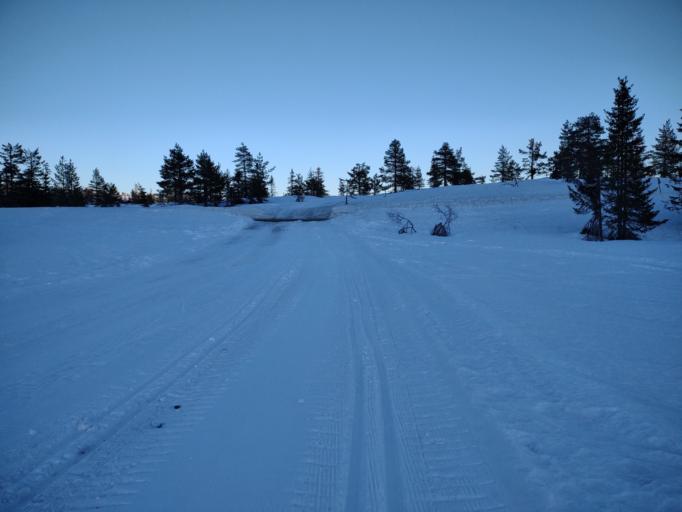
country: NO
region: Buskerud
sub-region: Flesberg
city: Lampeland
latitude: 59.7602
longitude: 9.4421
